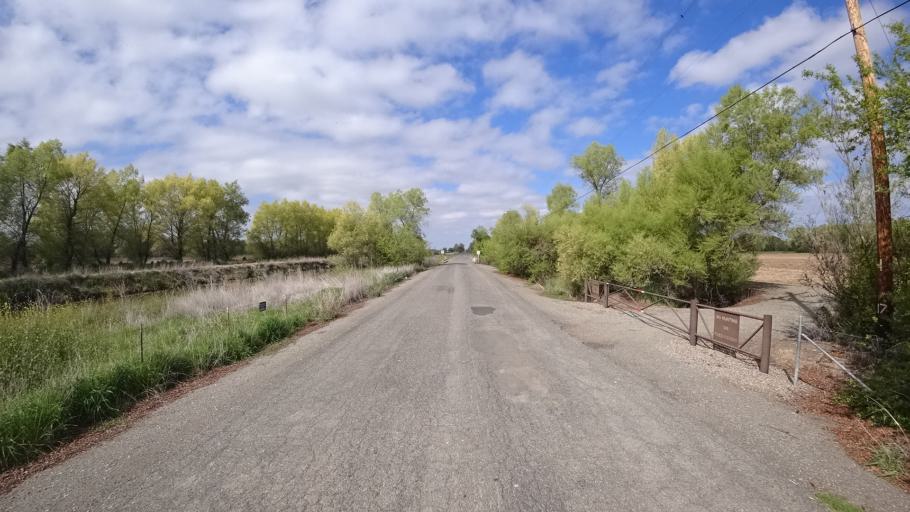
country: US
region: California
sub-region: Butte County
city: Biggs
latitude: 39.4199
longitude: -121.8936
